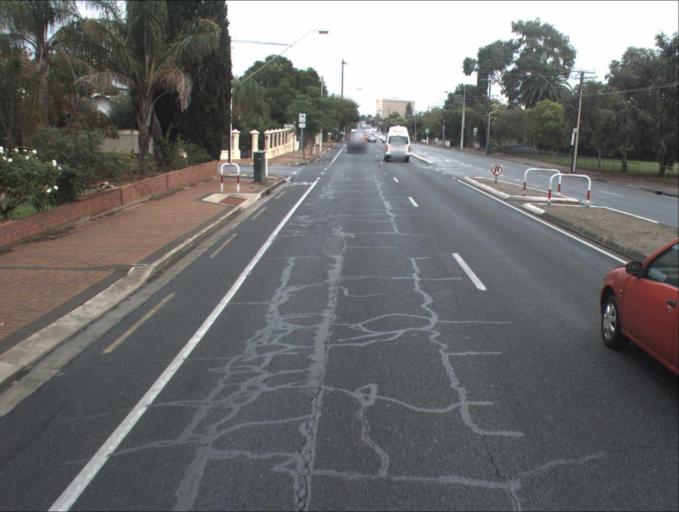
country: AU
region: South Australia
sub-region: Port Adelaide Enfield
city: Klemzig
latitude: -34.8808
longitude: 138.6244
